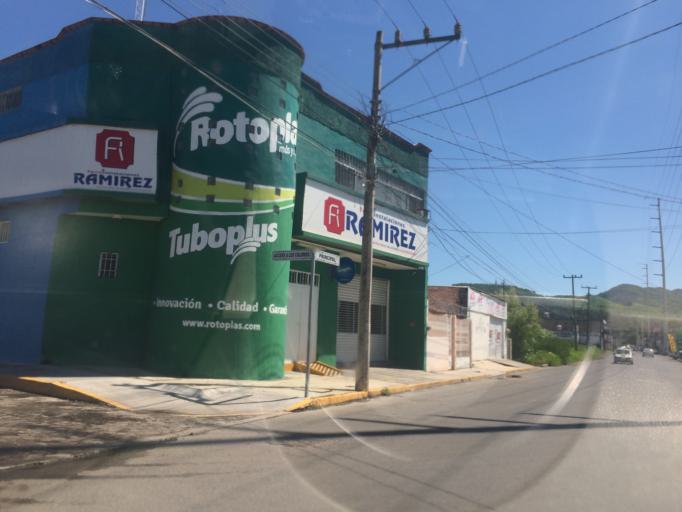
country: MX
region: Nayarit
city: Tepic
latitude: 21.4963
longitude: -104.8785
